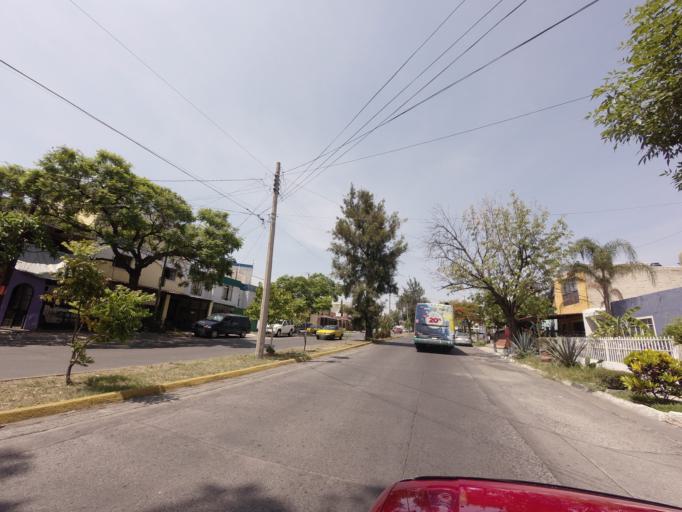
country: MX
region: Jalisco
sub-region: Zapopan
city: Zapopan
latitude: 20.6919
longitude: -103.3435
